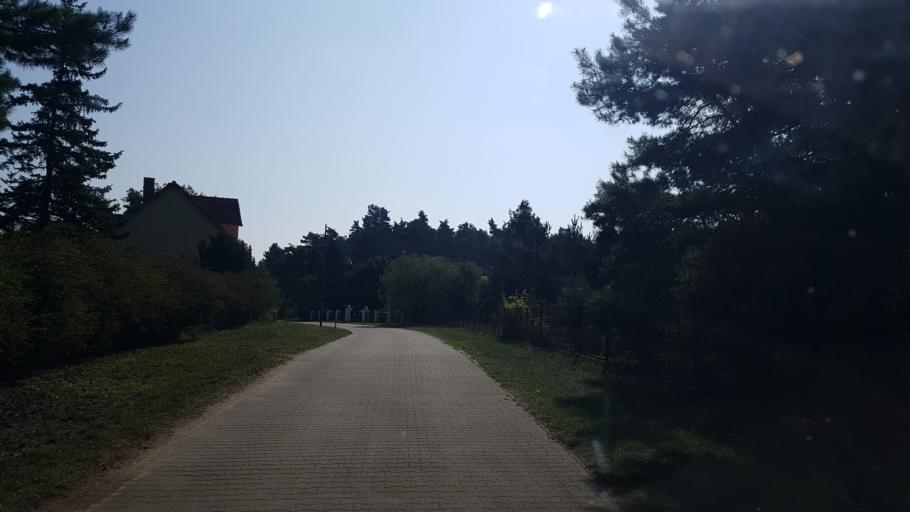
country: DE
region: Brandenburg
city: Luckau
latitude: 51.7988
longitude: 13.6412
